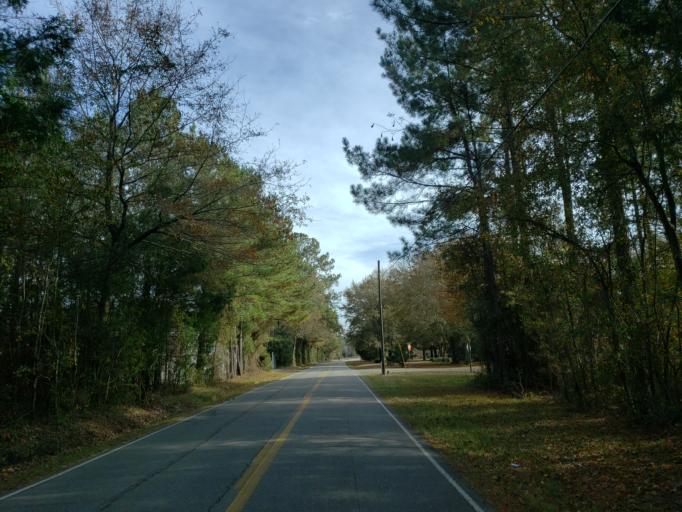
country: US
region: Mississippi
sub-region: Forrest County
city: Rawls Springs
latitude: 31.3923
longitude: -89.3829
